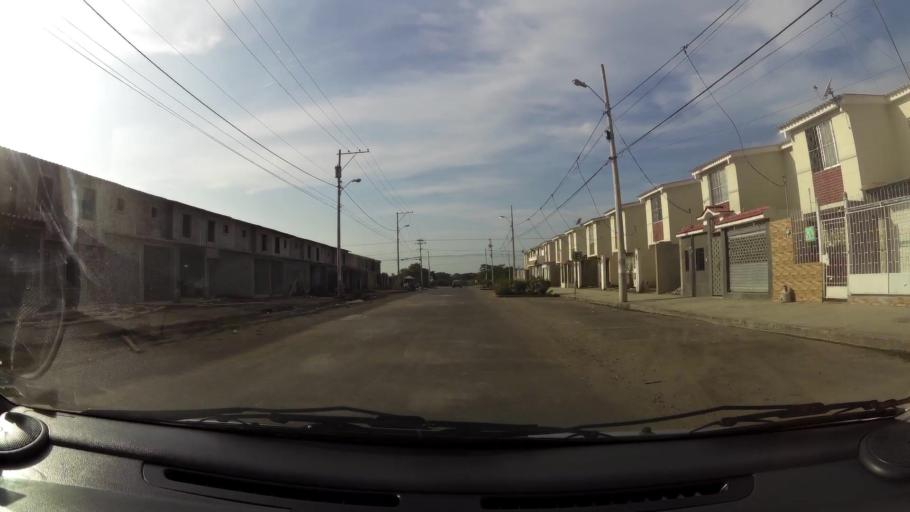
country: EC
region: Guayas
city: Eloy Alfaro
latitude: -2.0653
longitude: -79.8927
